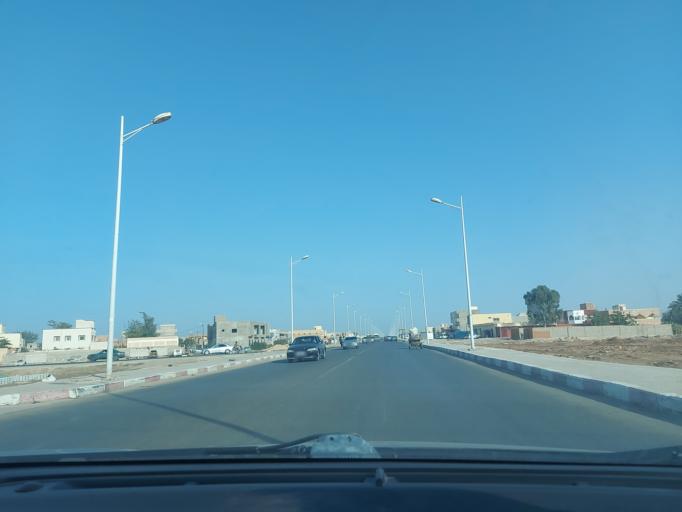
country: MR
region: Nouakchott
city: Nouakchott
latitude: 18.0861
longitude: -16.0023
